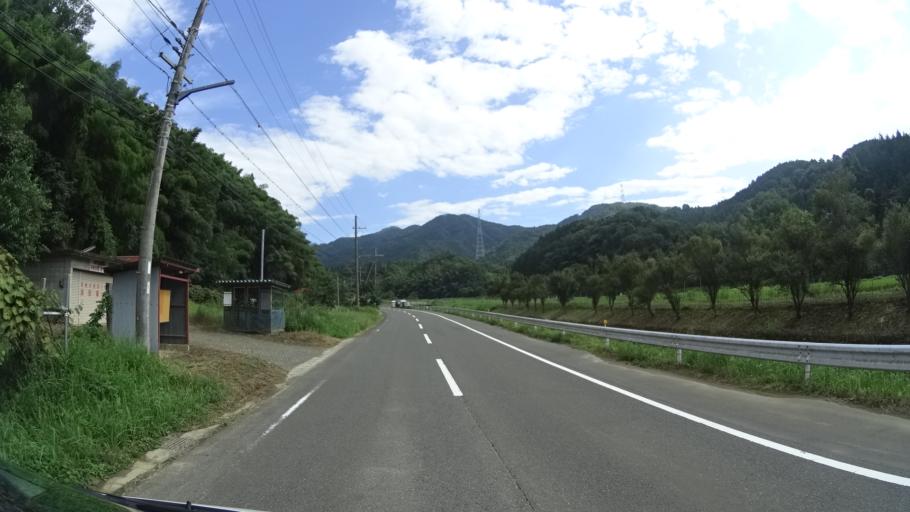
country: JP
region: Kyoto
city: Fukuchiyama
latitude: 35.3664
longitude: 135.1313
